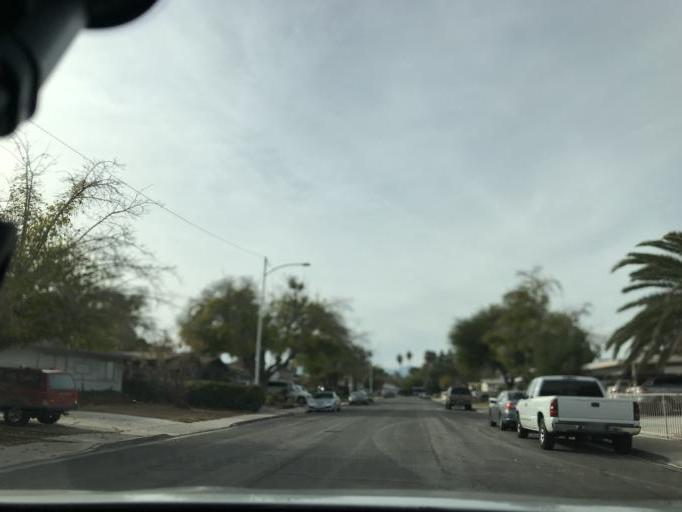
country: US
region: Nevada
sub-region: Clark County
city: Las Vegas
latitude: 36.1723
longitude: -115.1671
